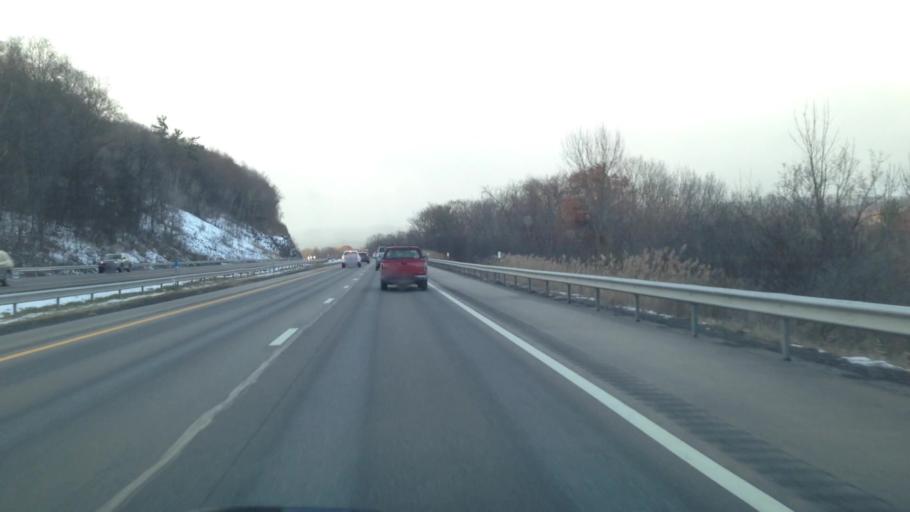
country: US
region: New York
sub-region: Schenectady County
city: Scotia
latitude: 42.8597
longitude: -74.0359
